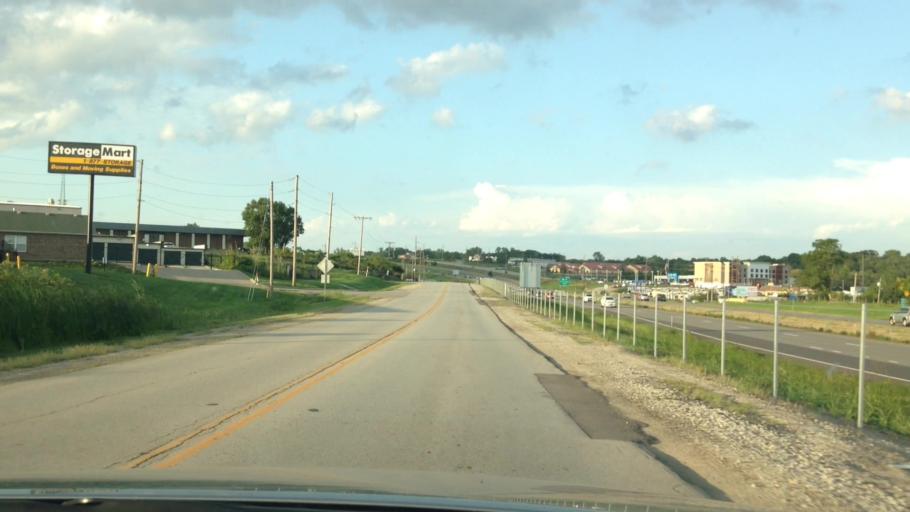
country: US
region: Missouri
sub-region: Clay County
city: Liberty
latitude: 39.2478
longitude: -94.4542
